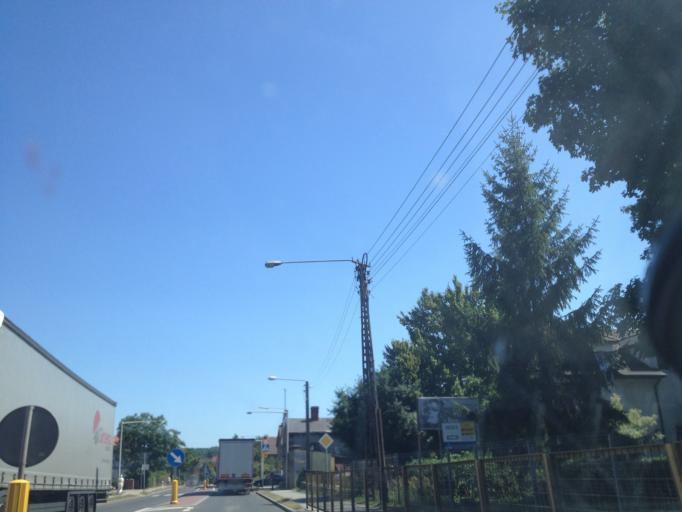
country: PL
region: Lubusz
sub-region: Powiat sulecinski
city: Torzym
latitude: 52.3140
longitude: 15.0717
